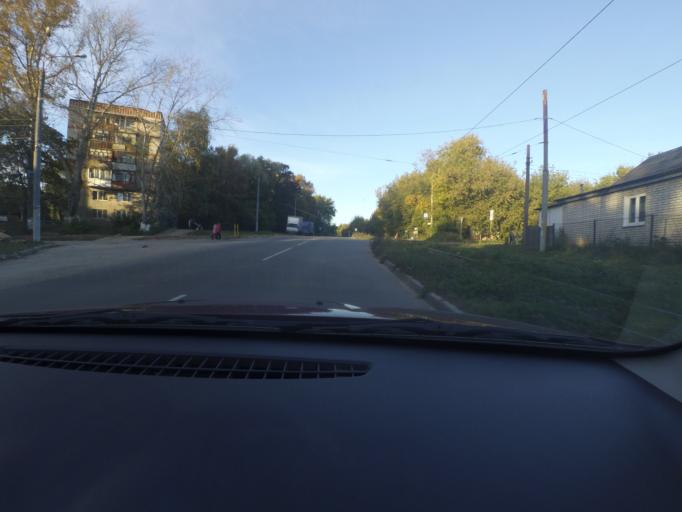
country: RU
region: Nizjnij Novgorod
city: Nizhniy Novgorod
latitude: 56.2788
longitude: 43.9902
